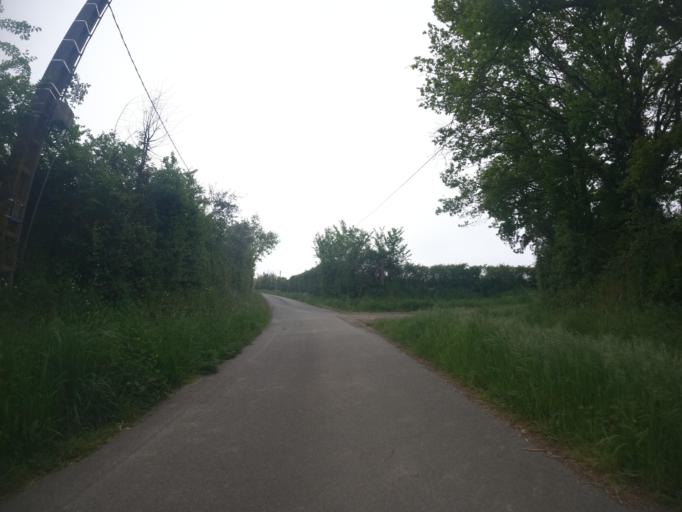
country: FR
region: Poitou-Charentes
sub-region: Departement des Deux-Sevres
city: Saint-Varent
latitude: 46.8895
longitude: -0.3144
